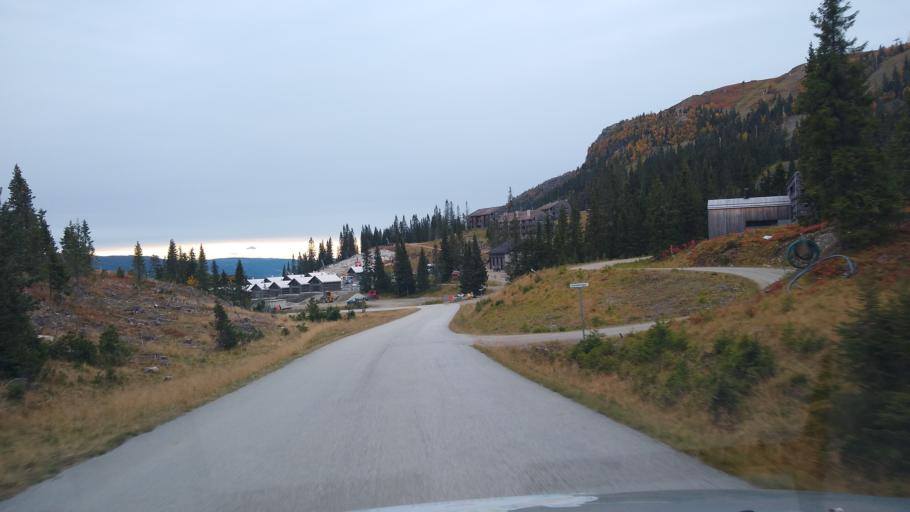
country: NO
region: Oppland
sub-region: Ringebu
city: Ringebu
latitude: 61.4750
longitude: 10.1288
